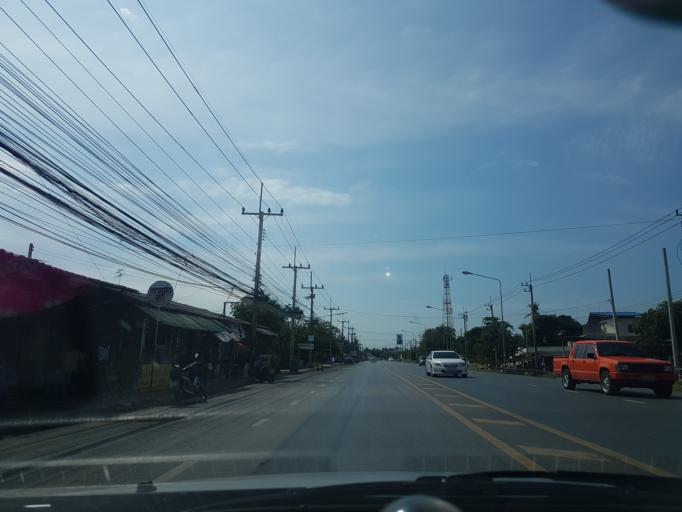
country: TH
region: Lop Buri
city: Lop Buri
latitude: 14.7839
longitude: 100.6946
